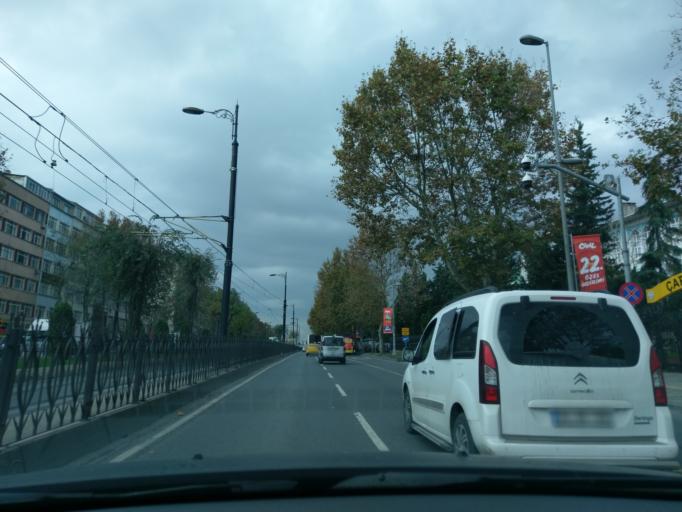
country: TR
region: Istanbul
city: Istanbul
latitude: 41.0141
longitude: 28.9361
